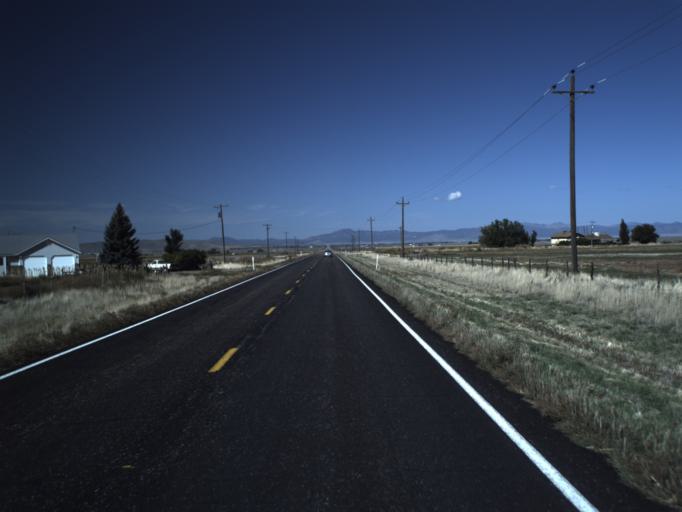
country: US
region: Utah
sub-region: Washington County
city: Enterprise
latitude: 37.6746
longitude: -113.5594
